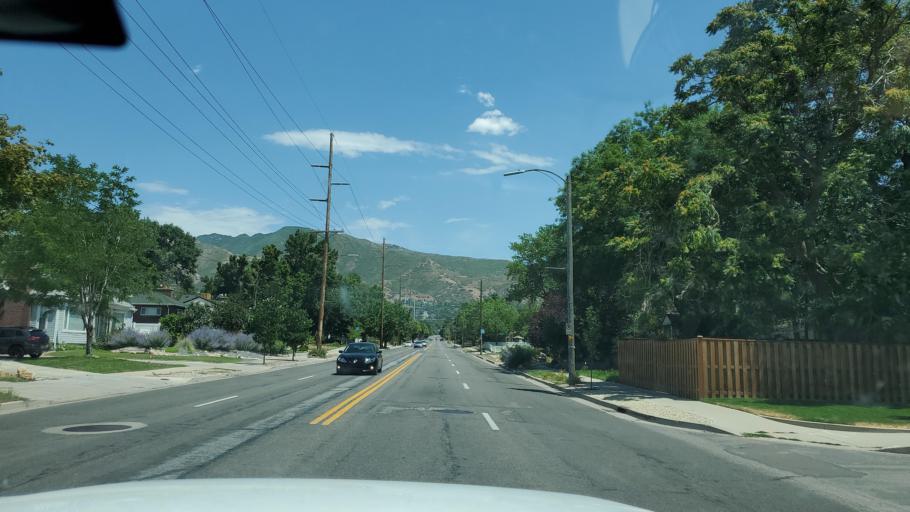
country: US
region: Utah
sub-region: Salt Lake County
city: Willard
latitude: 40.7255
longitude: -111.8408
